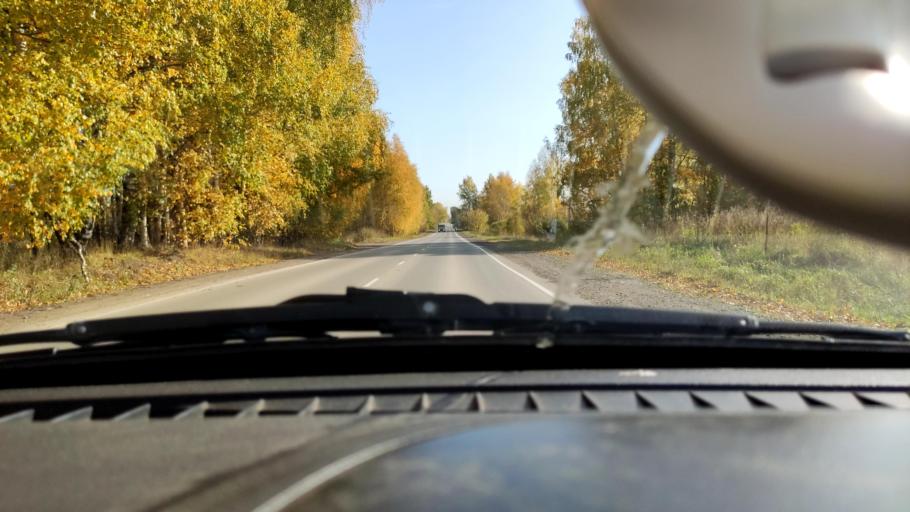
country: RU
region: Perm
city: Overyata
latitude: 58.0573
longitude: 55.8544
